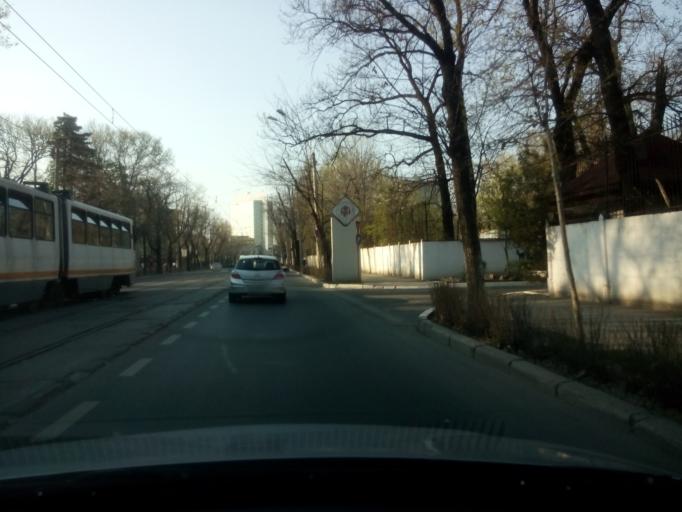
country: RO
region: Bucuresti
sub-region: Municipiul Bucuresti
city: Bucuresti
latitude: 44.4724
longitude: 26.0721
